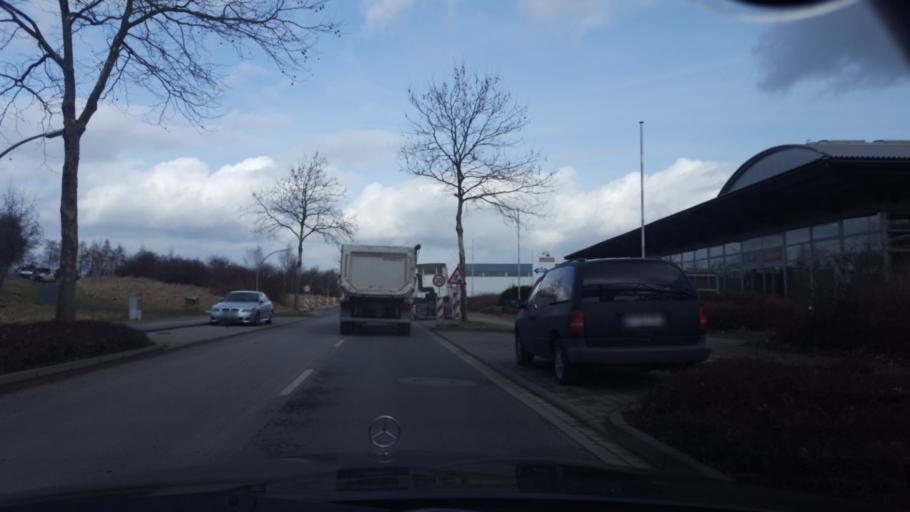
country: DE
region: North Rhine-Westphalia
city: Datteln
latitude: 51.6362
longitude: 7.3354
